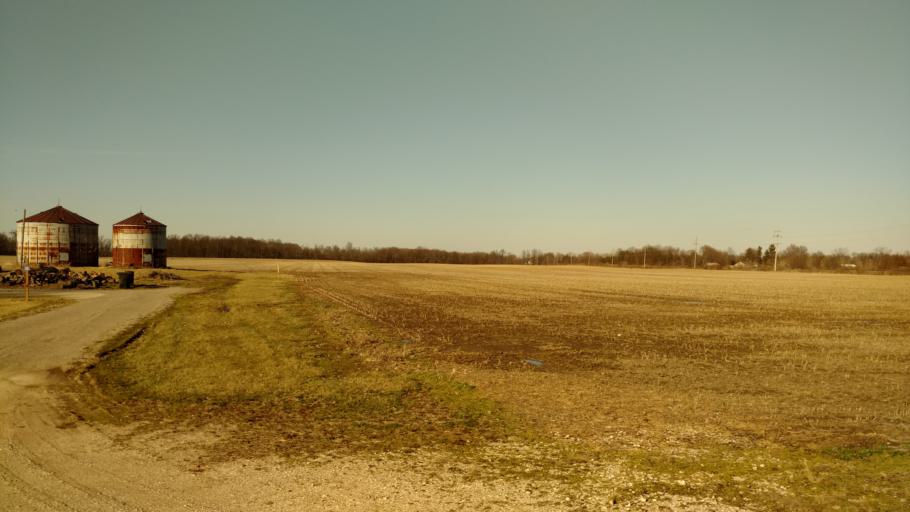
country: US
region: Ohio
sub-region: Crawford County
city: Galion
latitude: 40.6978
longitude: -82.7985
